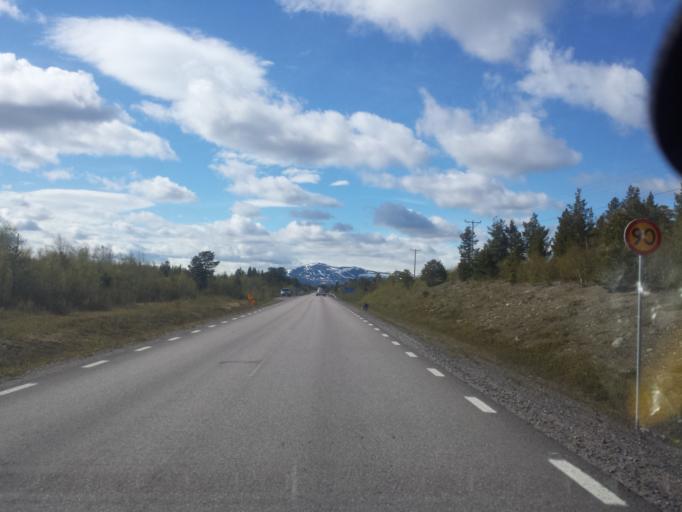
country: SE
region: Norrbotten
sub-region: Kiruna Kommun
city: Kiruna
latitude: 67.9894
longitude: 19.9287
